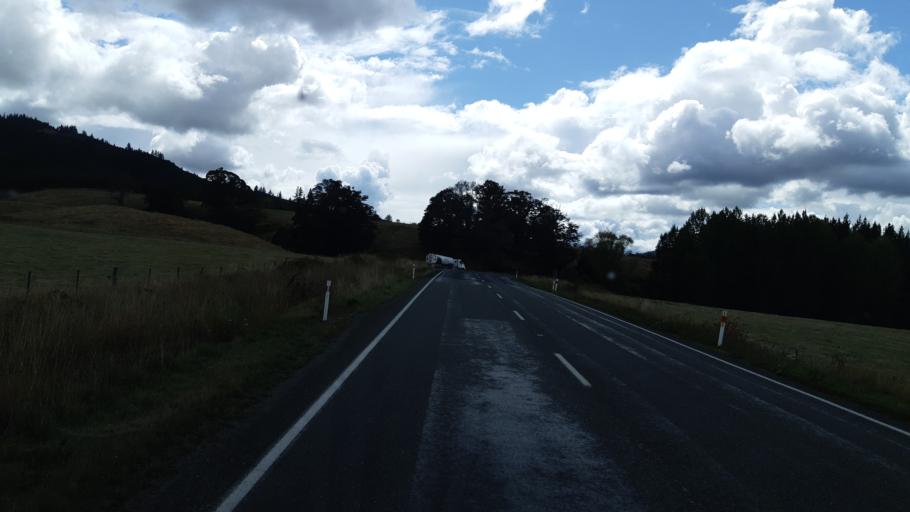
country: NZ
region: Tasman
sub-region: Tasman District
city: Wakefield
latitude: -41.5572
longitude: 172.7855
